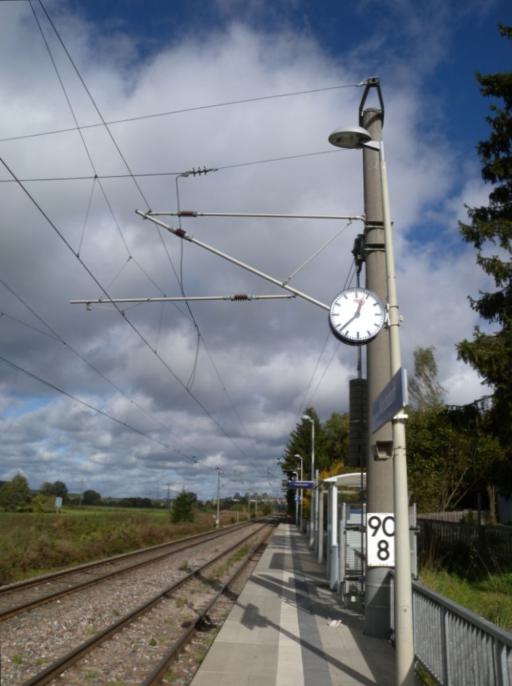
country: DE
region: Baden-Wuerttemberg
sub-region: Freiburg Region
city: Villingen-Schwenningen
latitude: 48.0146
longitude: 8.4679
